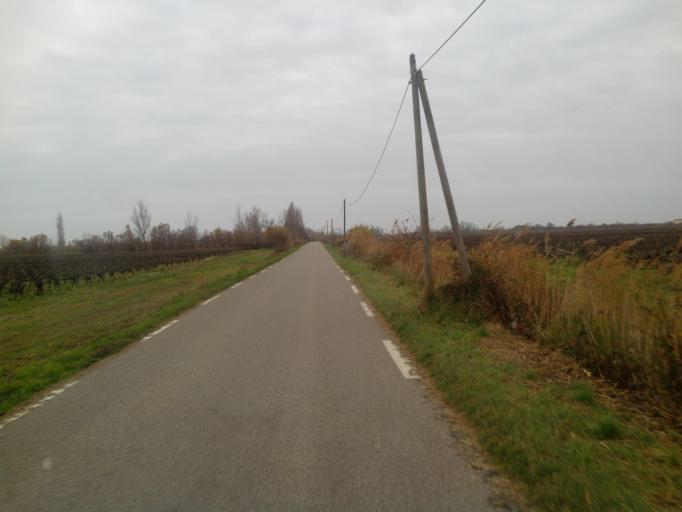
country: FR
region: Languedoc-Roussillon
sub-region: Departement du Gard
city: Vauvert
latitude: 43.5710
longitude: 4.3293
